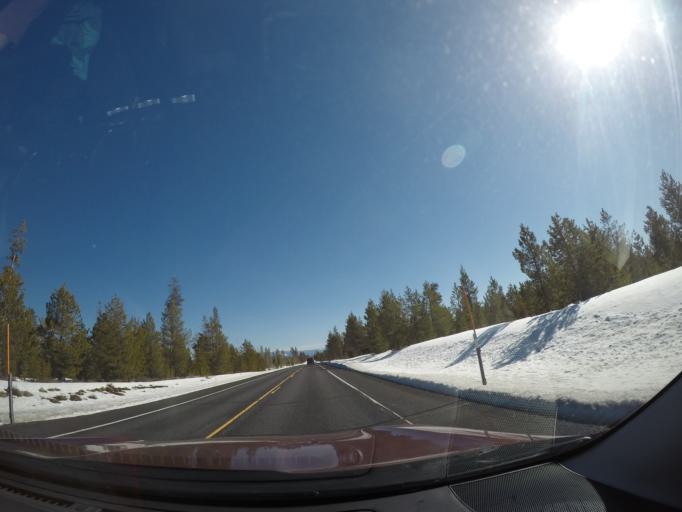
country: US
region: Oregon
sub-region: Deschutes County
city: Three Rivers
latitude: 43.8784
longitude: -121.5631
